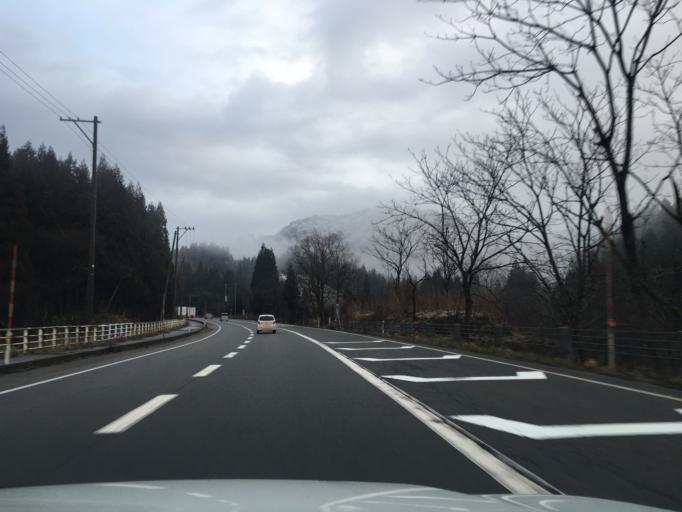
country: JP
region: Niigata
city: Murakami
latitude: 38.3739
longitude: 139.5559
